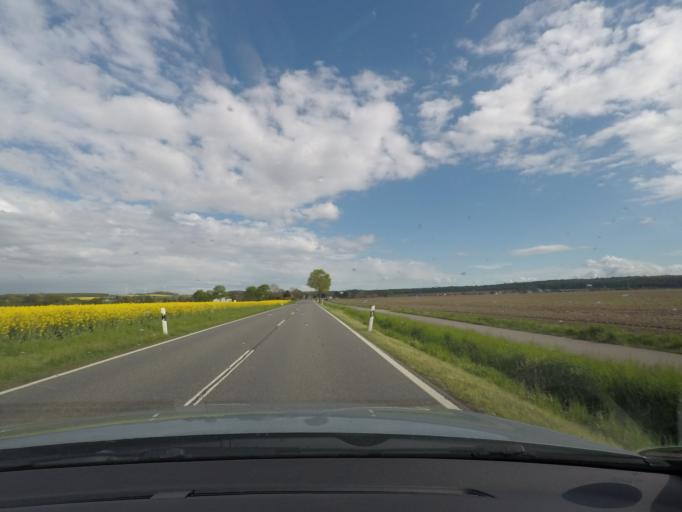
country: DE
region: Lower Saxony
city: Querenhorst
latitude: 52.3426
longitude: 10.9553
